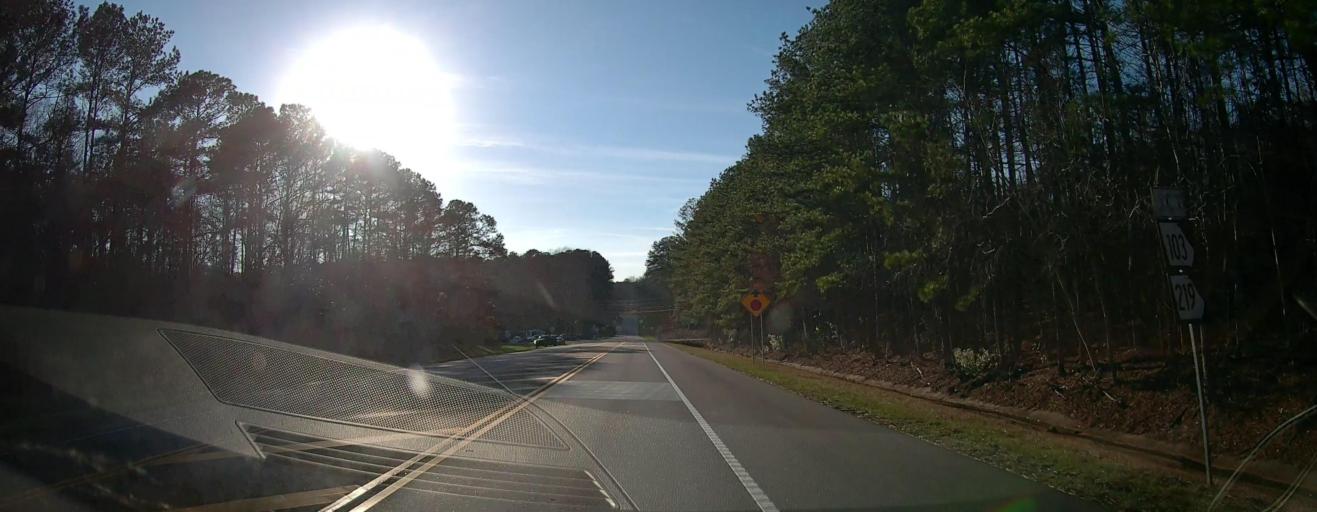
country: US
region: Georgia
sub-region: Harris County
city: Hamilton
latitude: 32.7472
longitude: -85.0191
